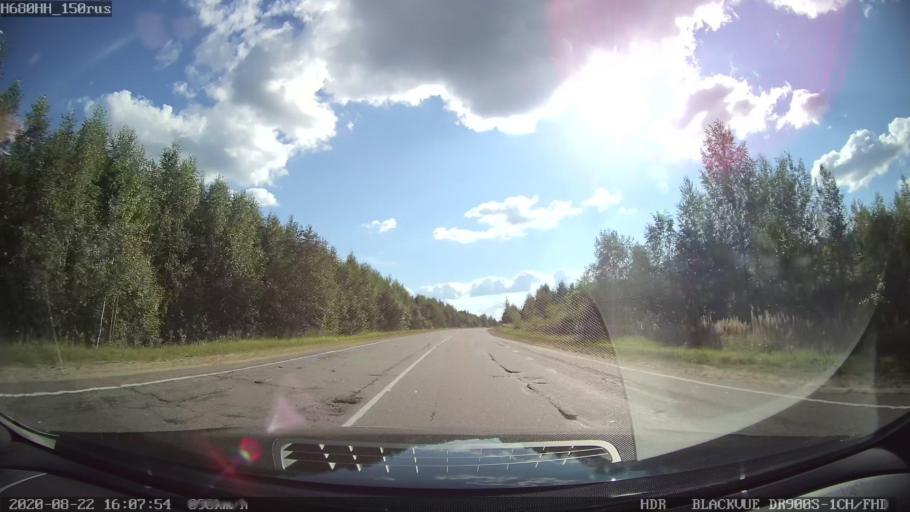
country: RU
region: Tverskaya
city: Rameshki
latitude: 57.5465
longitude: 36.3076
